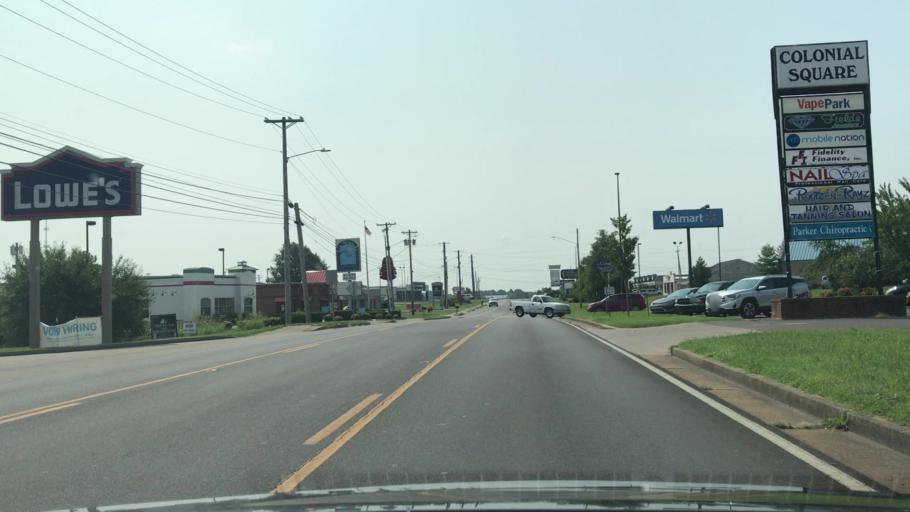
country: US
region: Kentucky
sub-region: Graves County
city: Mayfield
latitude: 36.7218
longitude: -88.6269
